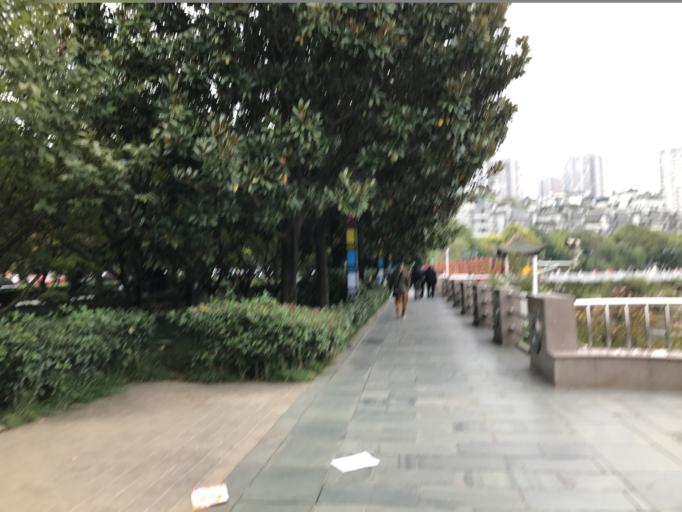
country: CN
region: Guizhou Sheng
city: Guiyang
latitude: 26.5751
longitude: 106.7149
